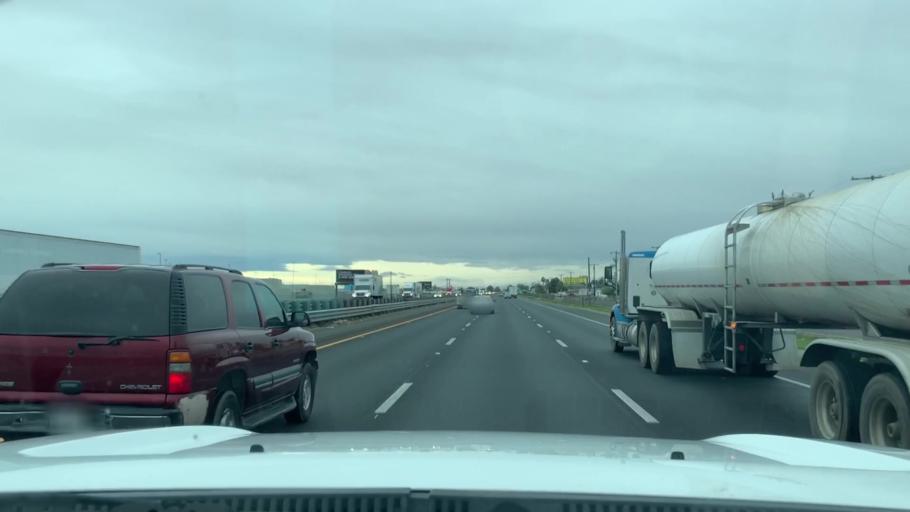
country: US
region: California
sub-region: Kern County
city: Delano
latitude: 35.7408
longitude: -119.2420
